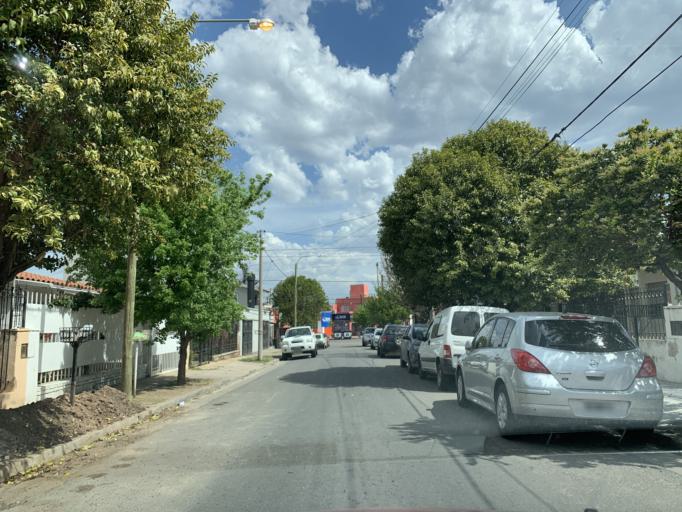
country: AR
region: Cordoba
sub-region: Departamento de Capital
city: Cordoba
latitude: -31.3623
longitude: -64.2276
